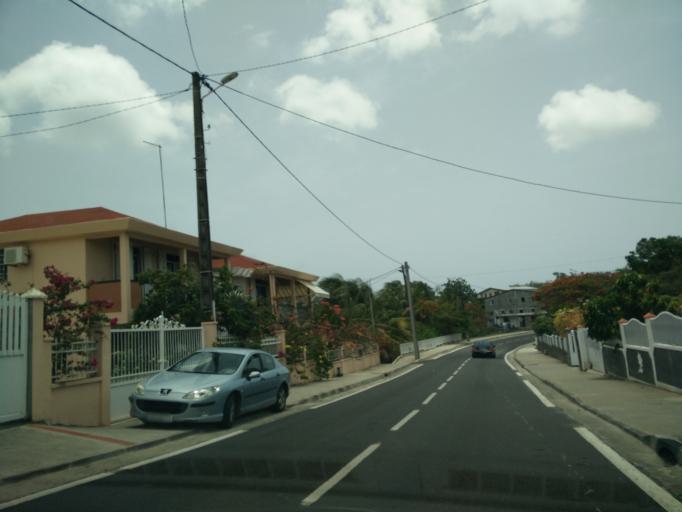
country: GP
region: Guadeloupe
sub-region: Guadeloupe
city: Anse-Bertrand
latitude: 16.4698
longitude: -61.5114
